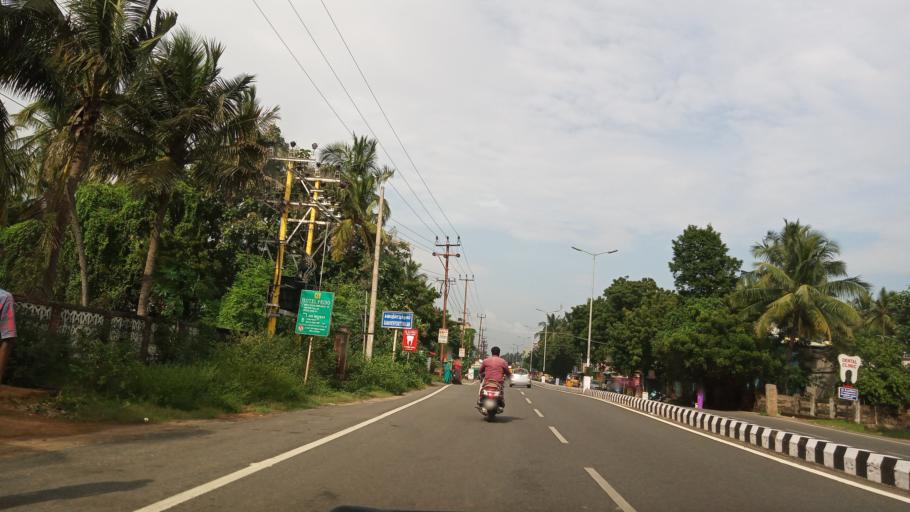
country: IN
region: Tamil Nadu
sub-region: Villupuram
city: Auroville
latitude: 12.0400
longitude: 79.8679
